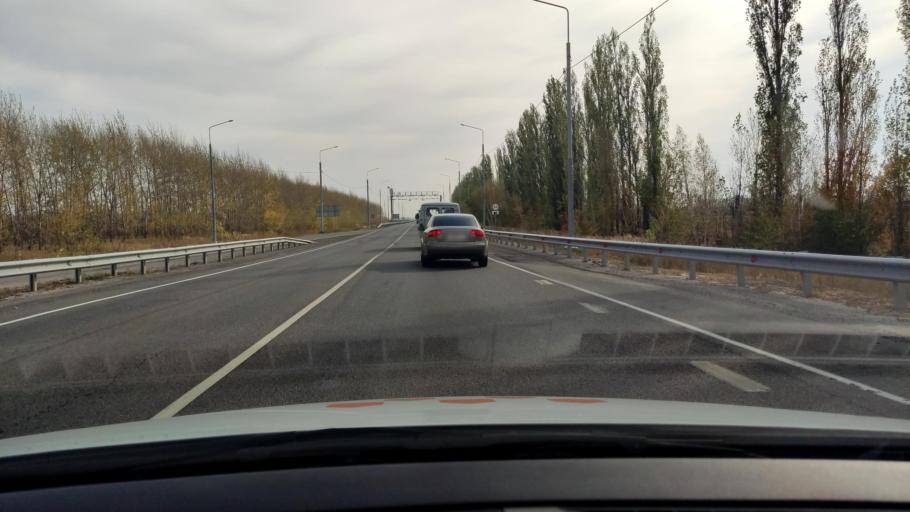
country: RU
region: Voronezj
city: Volya
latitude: 51.6894
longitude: 39.5026
